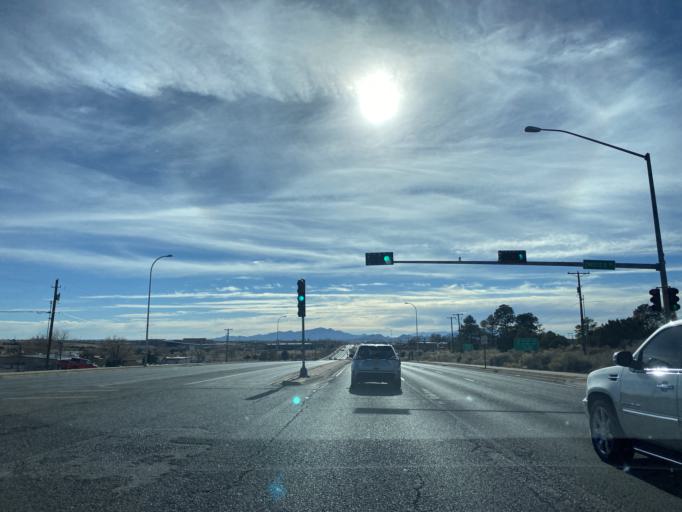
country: US
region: New Mexico
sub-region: Santa Fe County
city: Agua Fria
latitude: 35.6304
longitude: -106.0227
